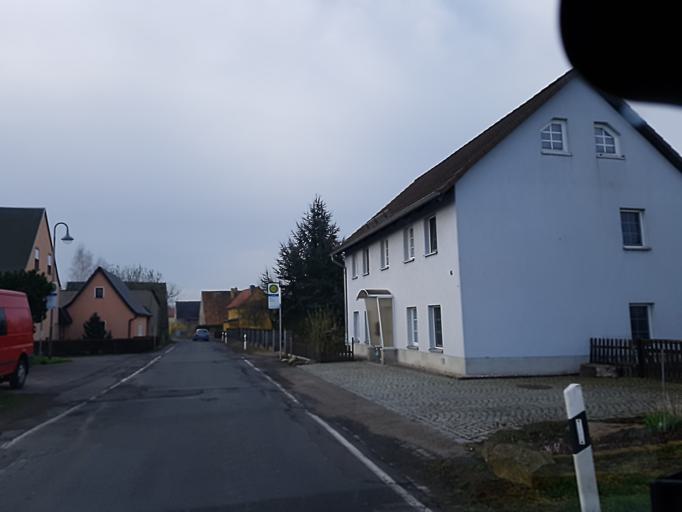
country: DE
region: Saxony
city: Naundorf
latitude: 51.2419
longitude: 13.1256
